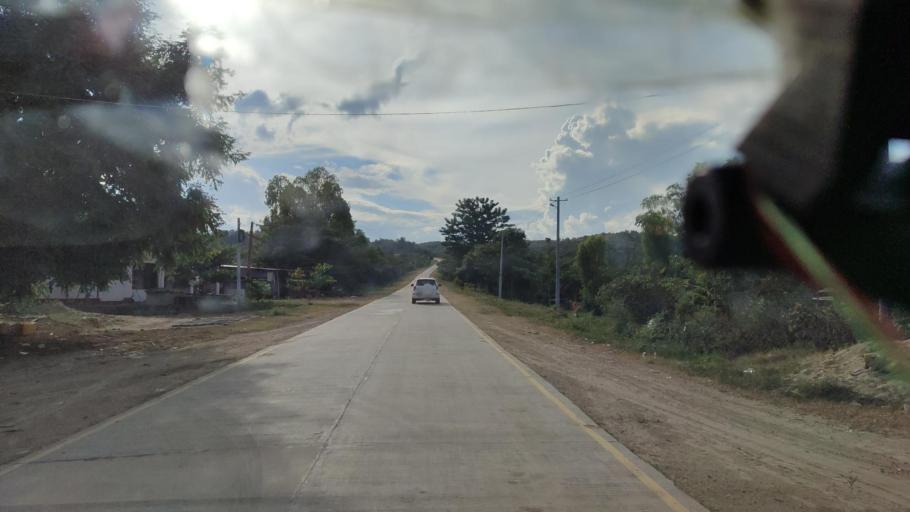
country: MM
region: Mandalay
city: Yamethin
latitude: 20.1390
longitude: 96.0910
